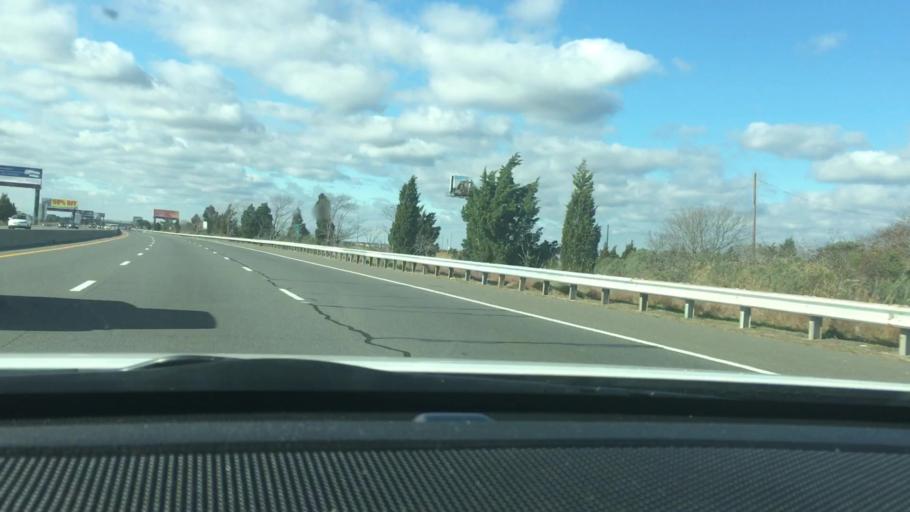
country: US
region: New Jersey
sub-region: Atlantic County
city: Ventnor City
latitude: 39.3698
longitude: -74.4646
